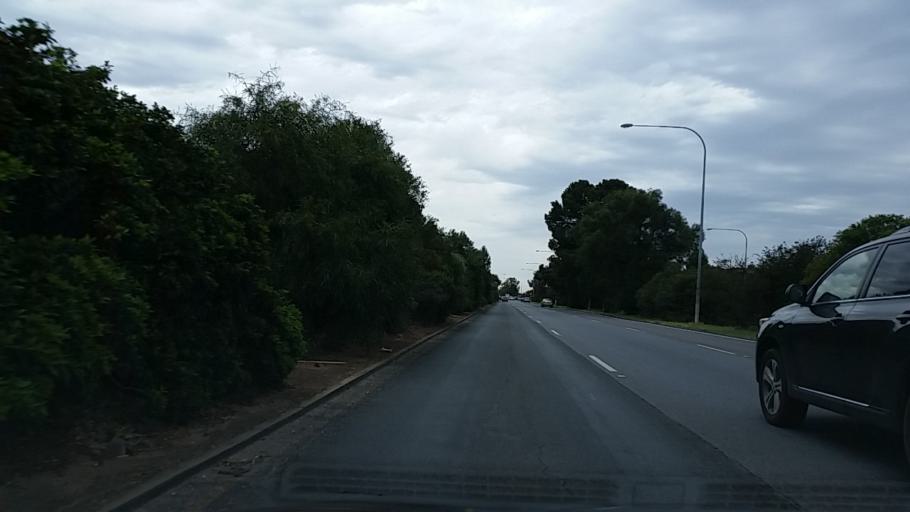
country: AU
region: South Australia
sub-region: Salisbury
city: Elizabeth
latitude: -34.7103
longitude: 138.6765
